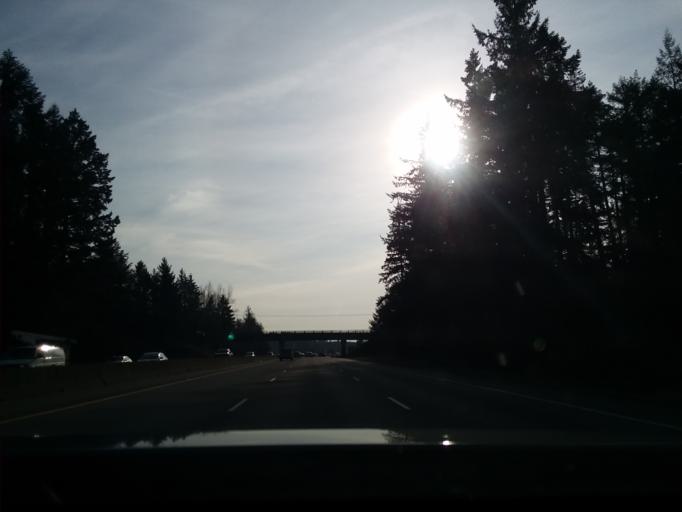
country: US
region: Washington
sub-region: Thurston County
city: Tumwater
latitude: 46.9251
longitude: -122.9458
